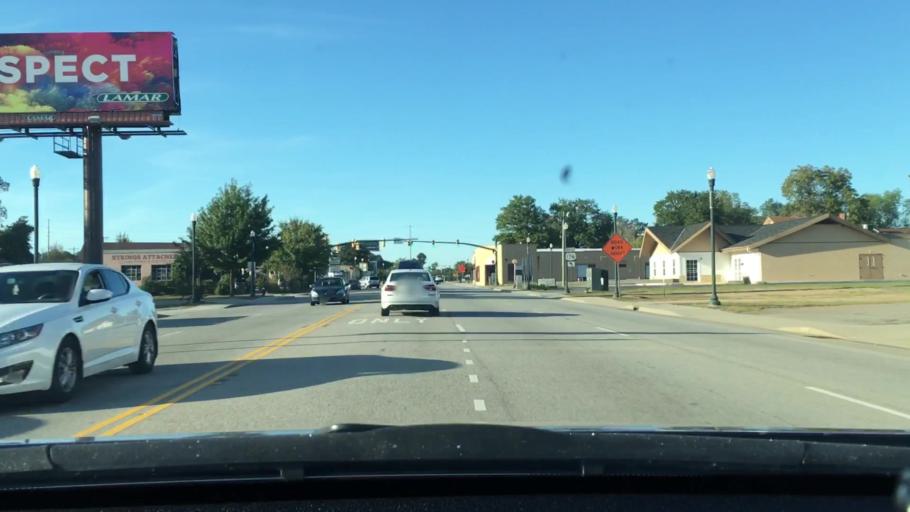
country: US
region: South Carolina
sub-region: Richland County
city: Columbia
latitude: 34.0191
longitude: -81.0415
